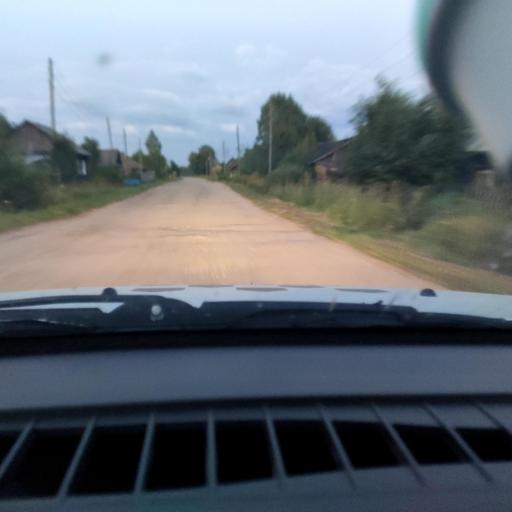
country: RU
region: Kirov
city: Darovskoy
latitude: 58.9895
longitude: 47.8691
